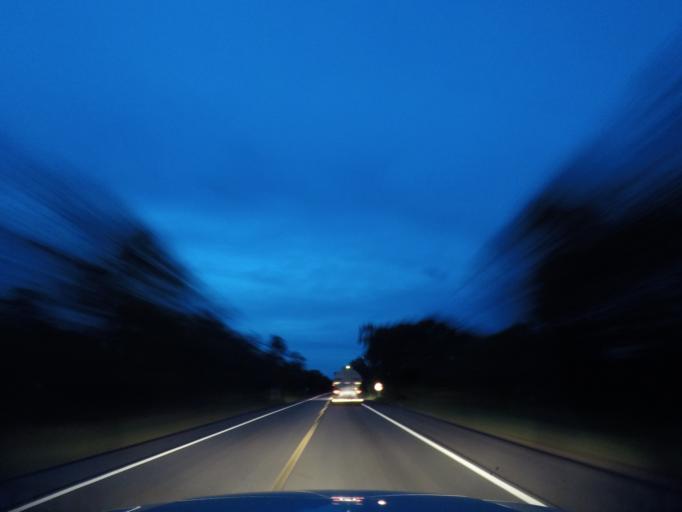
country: BR
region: Bahia
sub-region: Andarai
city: Vera Cruz
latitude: -12.4867
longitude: -41.3433
